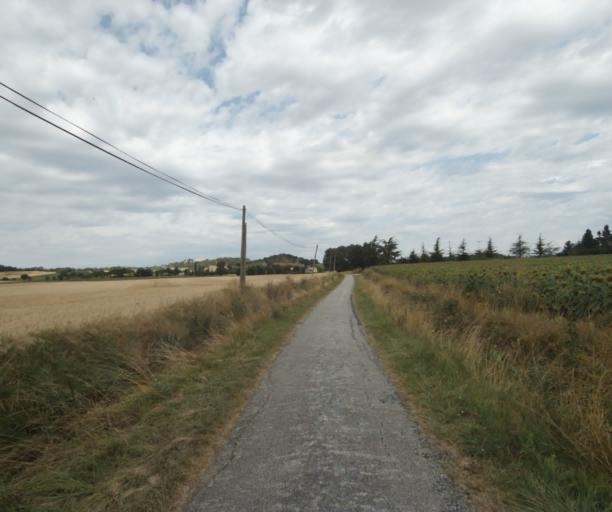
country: FR
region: Midi-Pyrenees
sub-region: Departement de la Haute-Garonne
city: Saint-Felix-Lauragais
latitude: 43.4393
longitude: 1.9122
